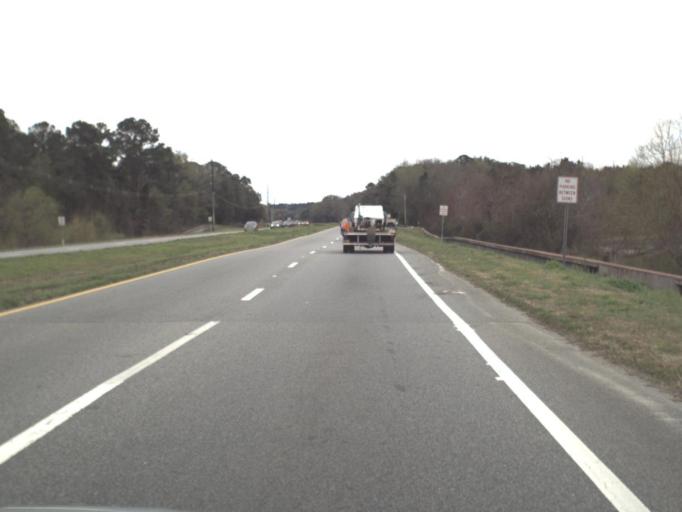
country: US
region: Florida
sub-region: Gadsden County
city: Midway
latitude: 30.5289
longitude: -84.3589
